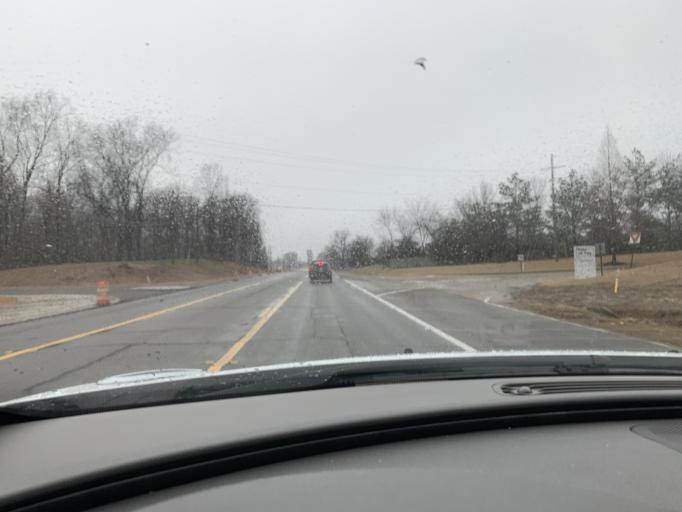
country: US
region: Mississippi
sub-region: De Soto County
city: Horn Lake
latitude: 34.9181
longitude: -90.0058
